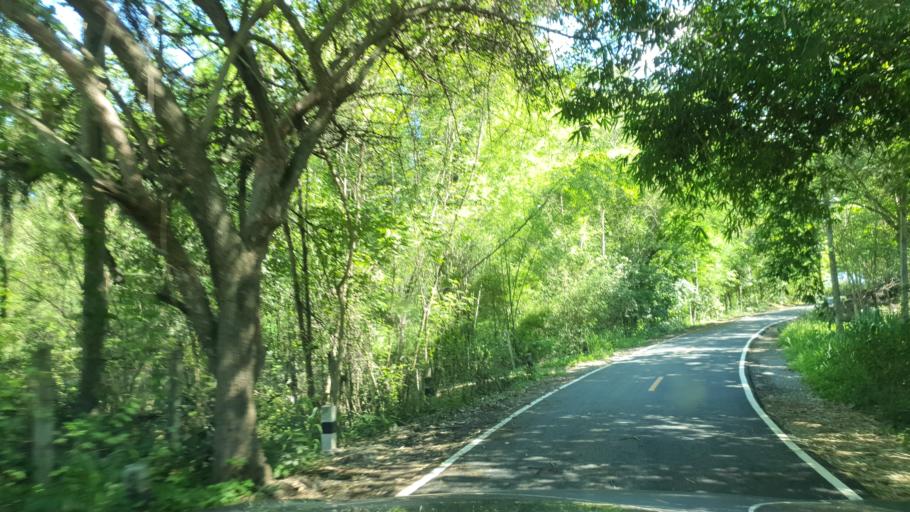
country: TH
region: Chiang Mai
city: Mae On
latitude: 18.7744
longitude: 99.2504
